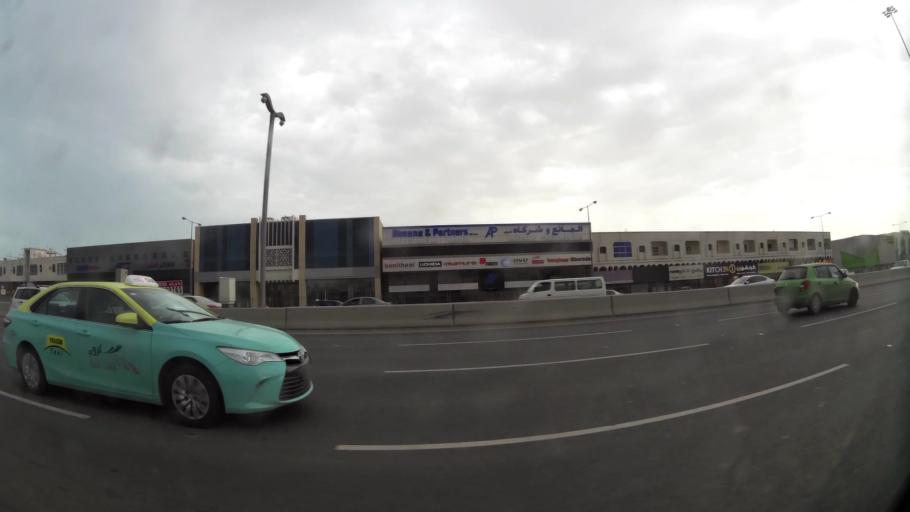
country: QA
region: Baladiyat ad Dawhah
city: Doha
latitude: 25.2597
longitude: 51.4898
